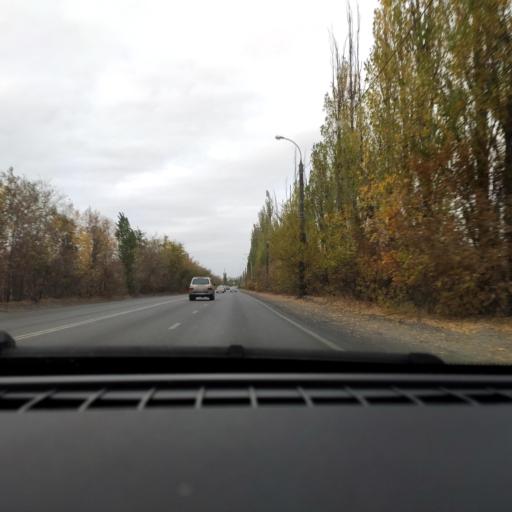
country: RU
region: Voronezj
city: Maslovka
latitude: 51.6088
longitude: 39.2561
